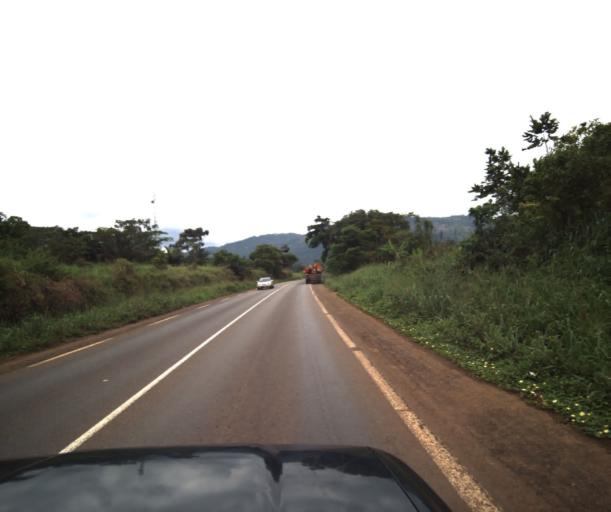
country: CM
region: Centre
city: Eseka
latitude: 3.8852
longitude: 10.8018
